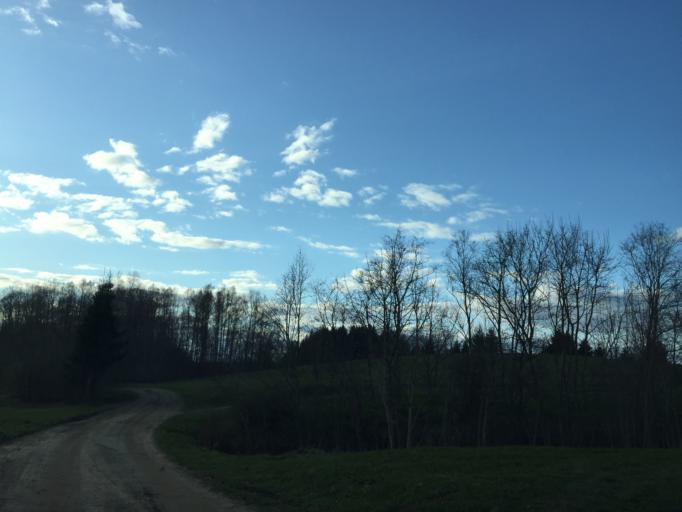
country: LV
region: Rezekne
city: Rezekne
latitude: 56.5819
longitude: 27.3580
